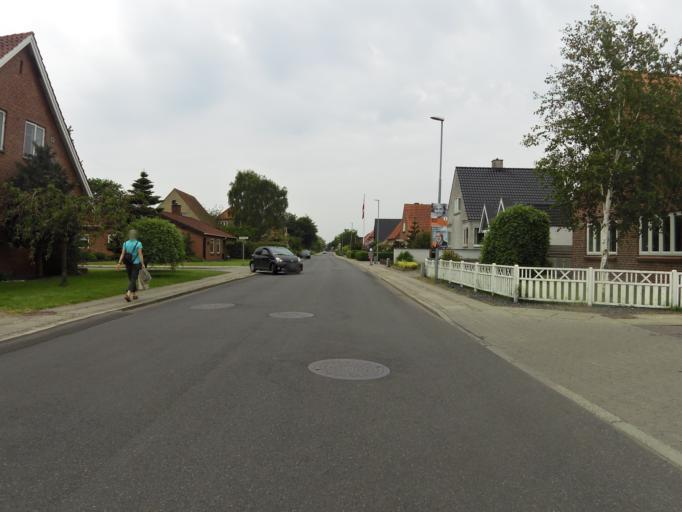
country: DK
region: South Denmark
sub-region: Esbjerg Kommune
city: Ribe
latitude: 55.3275
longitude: 8.7828
